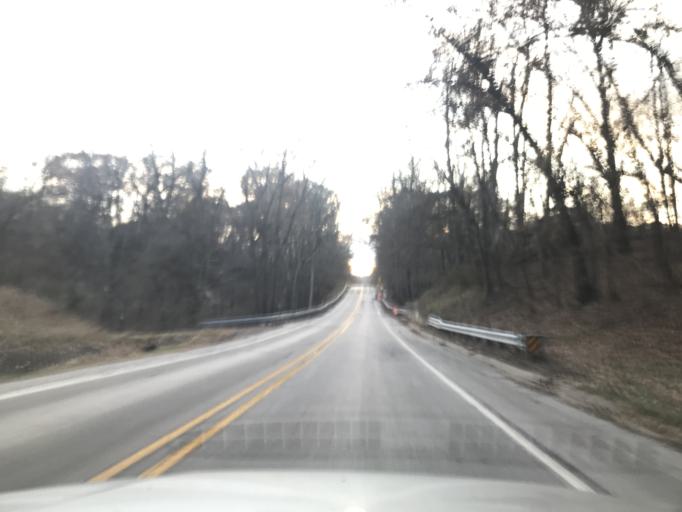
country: US
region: Illinois
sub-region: Henderson County
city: Oquawka
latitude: 40.9915
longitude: -90.8554
